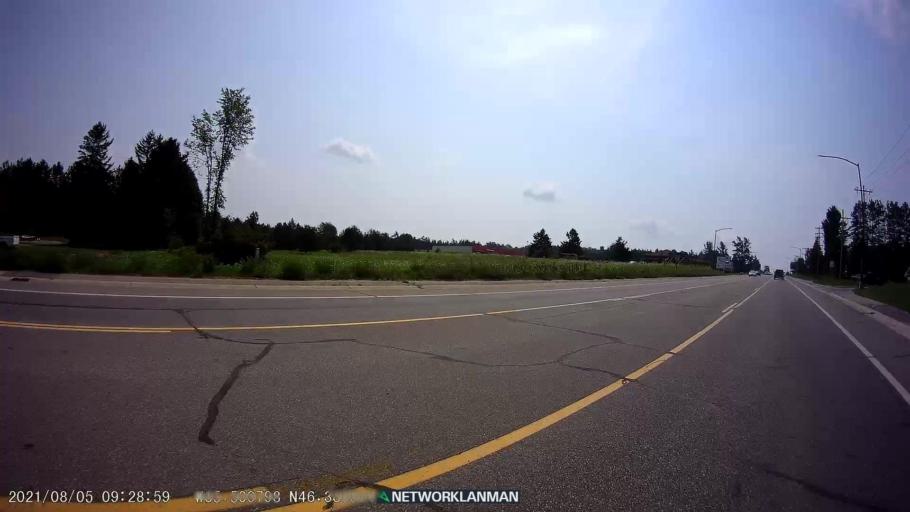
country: US
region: Michigan
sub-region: Luce County
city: Newberry
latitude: 46.3382
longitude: -85.5098
